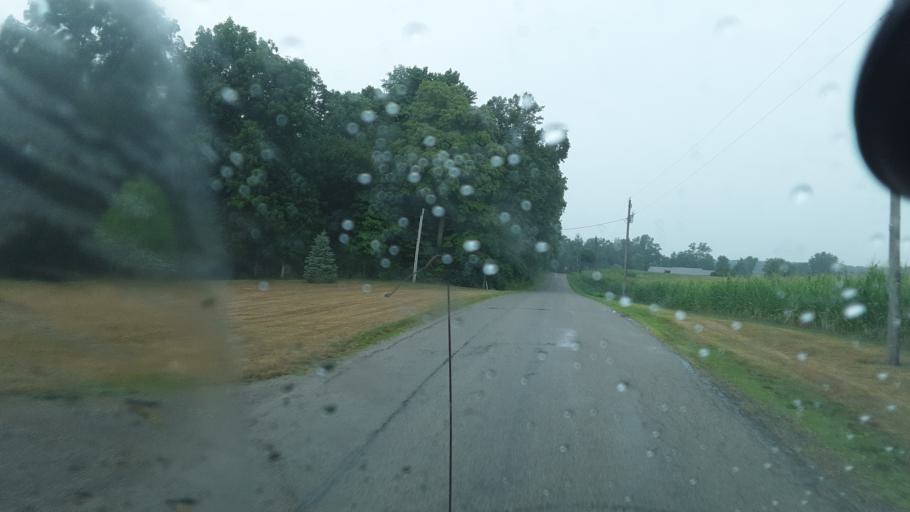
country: US
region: Ohio
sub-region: Williams County
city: Edgerton
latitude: 41.4269
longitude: -84.8078
